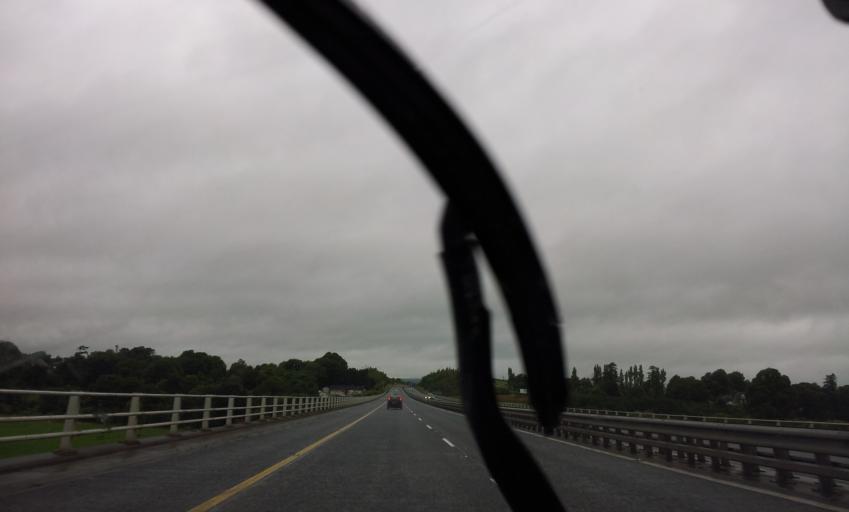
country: IE
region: Munster
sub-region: County Cork
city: Fermoy
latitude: 52.1381
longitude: -8.2615
